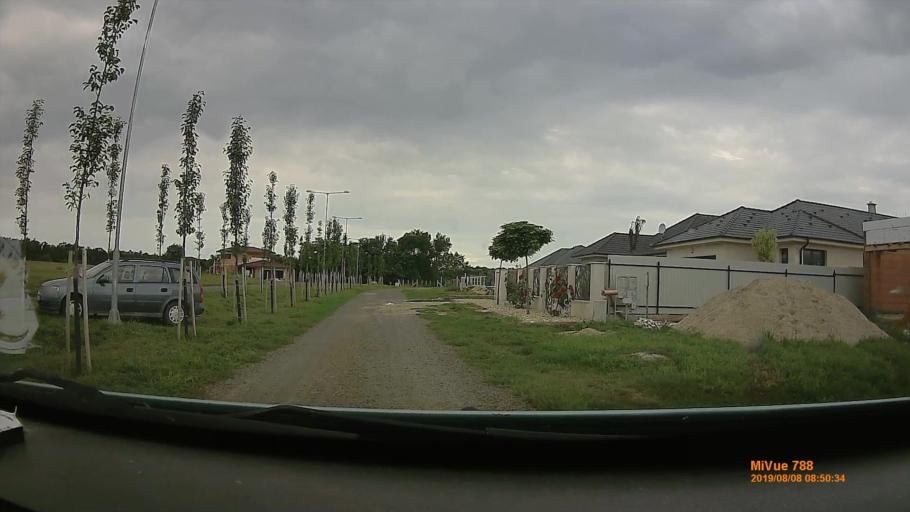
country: HU
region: Hajdu-Bihar
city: Debrecen
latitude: 47.6010
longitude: 21.6435
